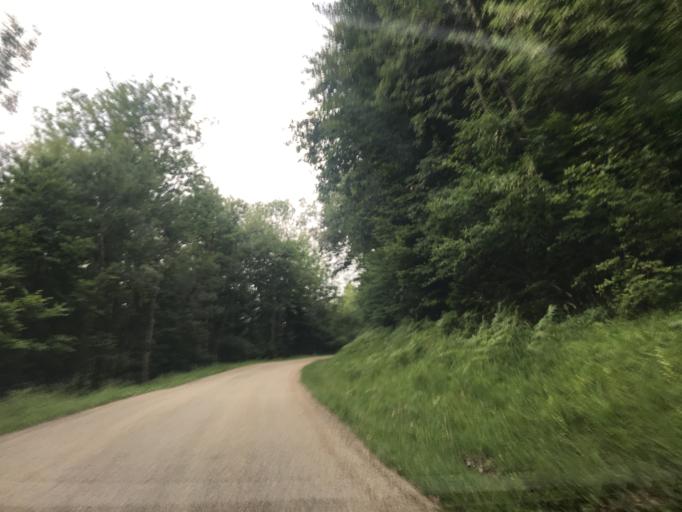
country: FR
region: Rhone-Alpes
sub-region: Departement de l'Isere
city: Saint-Vincent-de-Mercuze
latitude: 45.3735
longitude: 5.9230
